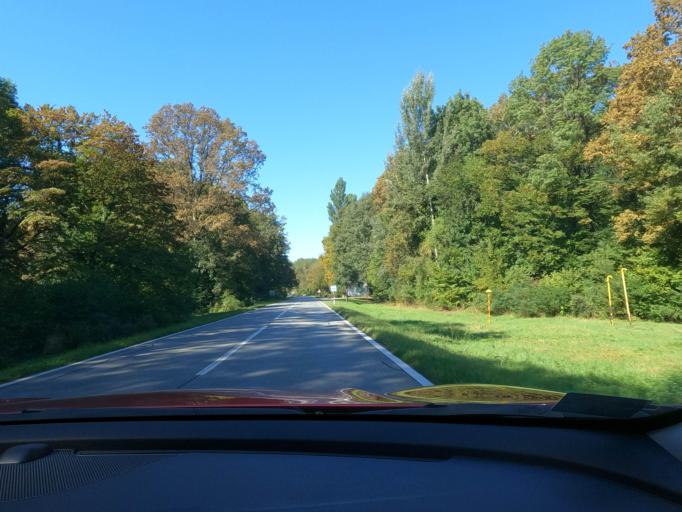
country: HR
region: Sisacko-Moslavacka
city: Budasevo
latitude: 45.4916
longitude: 16.4940
